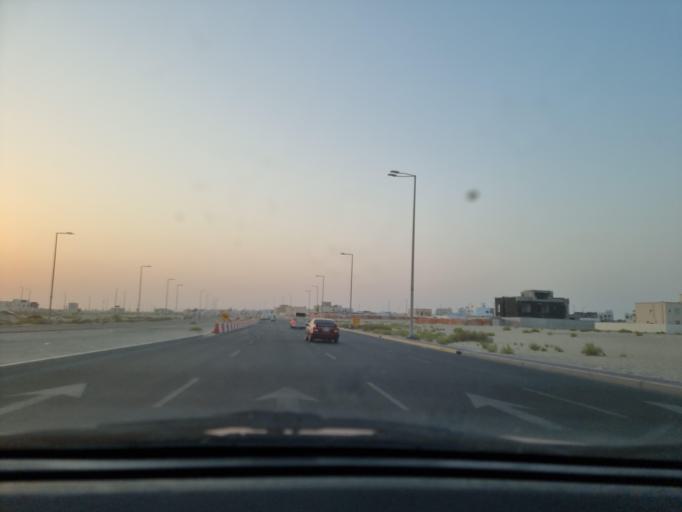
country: AE
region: Abu Dhabi
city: Abu Dhabi
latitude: 24.3659
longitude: 54.7539
